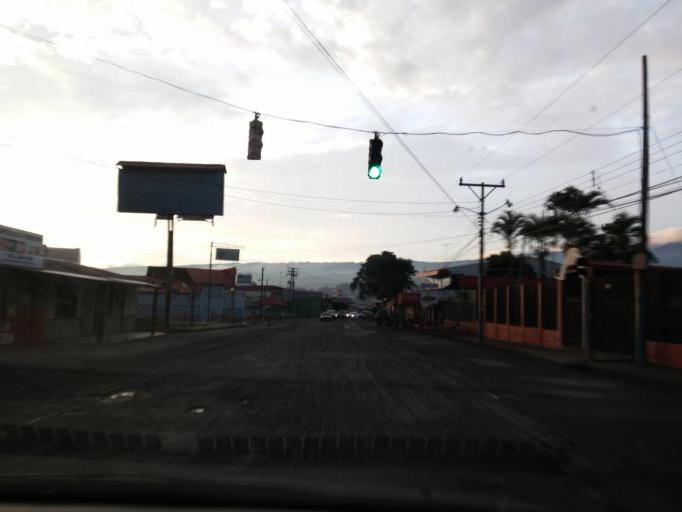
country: CR
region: Alajuela
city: San Juan
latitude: 10.0830
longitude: -84.3406
